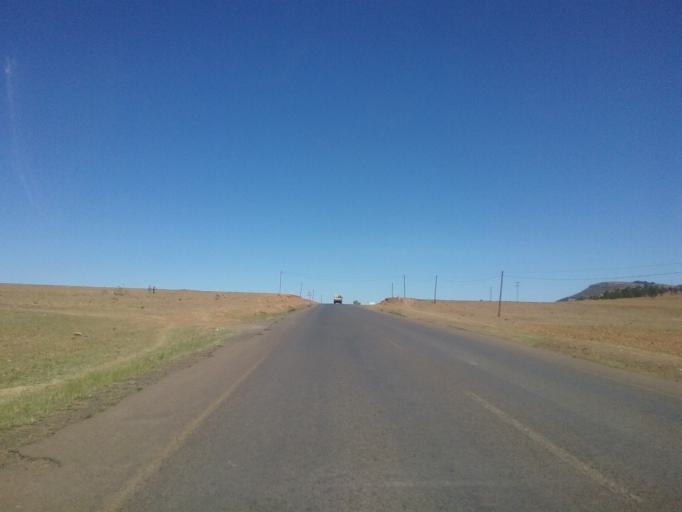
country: LS
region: Quthing
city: Quthing
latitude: -30.3936
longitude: 27.6341
